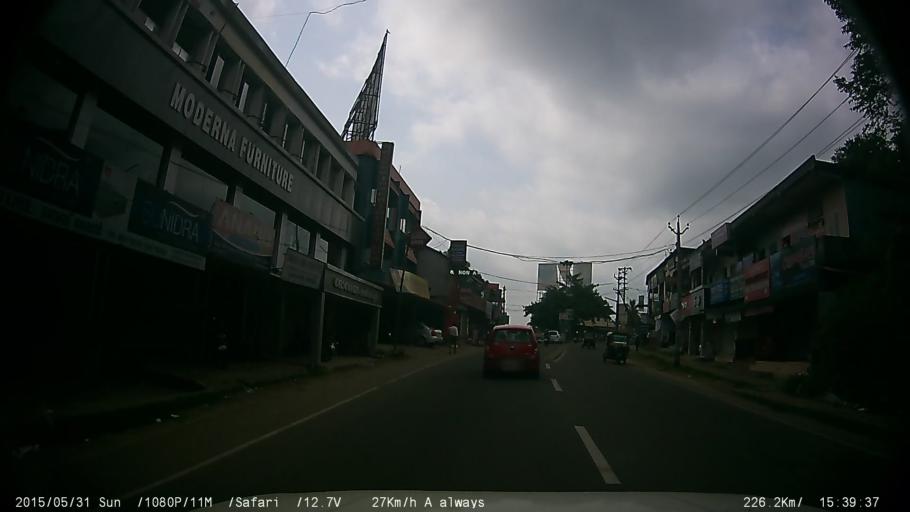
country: IN
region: Kerala
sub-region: Wayanad
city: Panamaram
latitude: 11.6658
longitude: 76.2628
